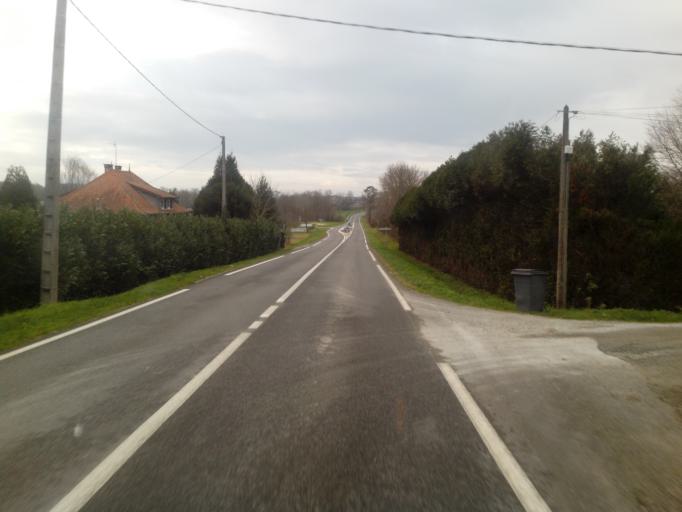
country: FR
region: Limousin
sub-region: Departement de la Haute-Vienne
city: Magnac-Laval
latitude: 46.2143
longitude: 1.1540
